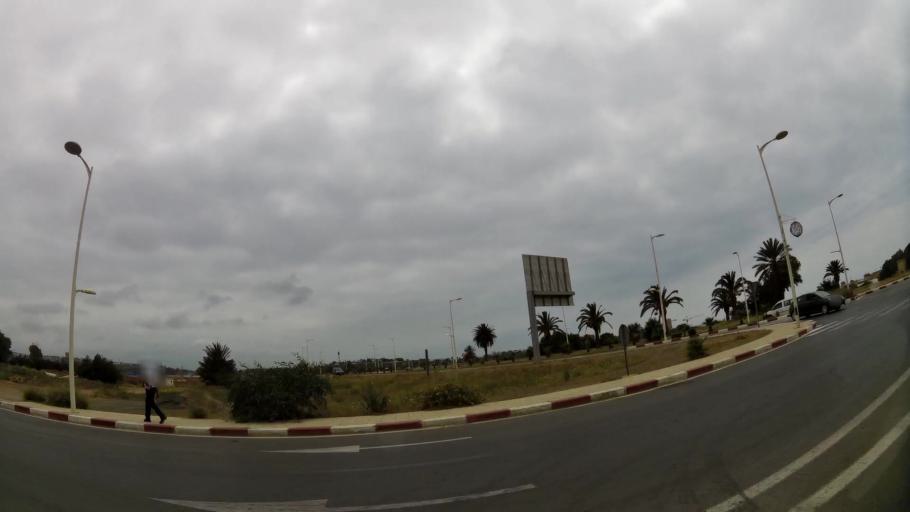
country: MA
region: Rabat-Sale-Zemmour-Zaer
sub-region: Rabat
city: Rabat
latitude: 34.0229
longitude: -6.8040
